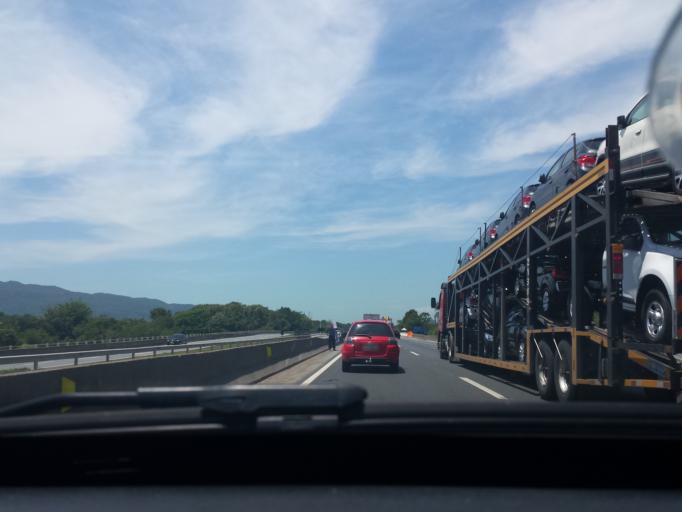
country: BR
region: Santa Catarina
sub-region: Itapema
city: Itapema
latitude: -27.1345
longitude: -48.6099
